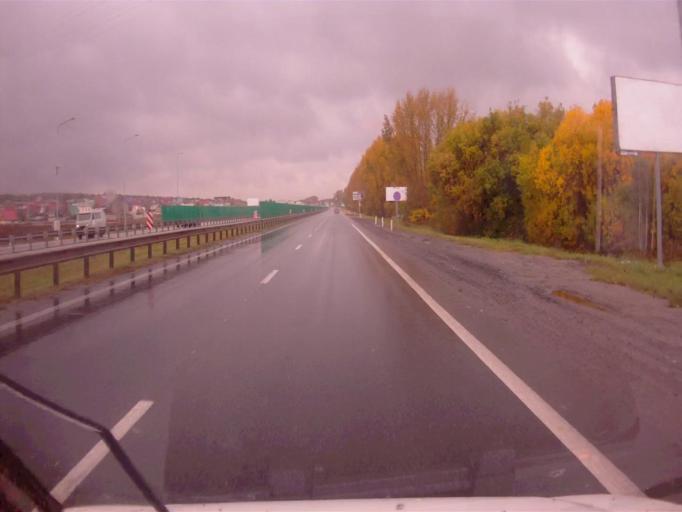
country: RU
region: Chelyabinsk
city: Dolgoderevenskoye
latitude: 55.2778
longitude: 61.3436
